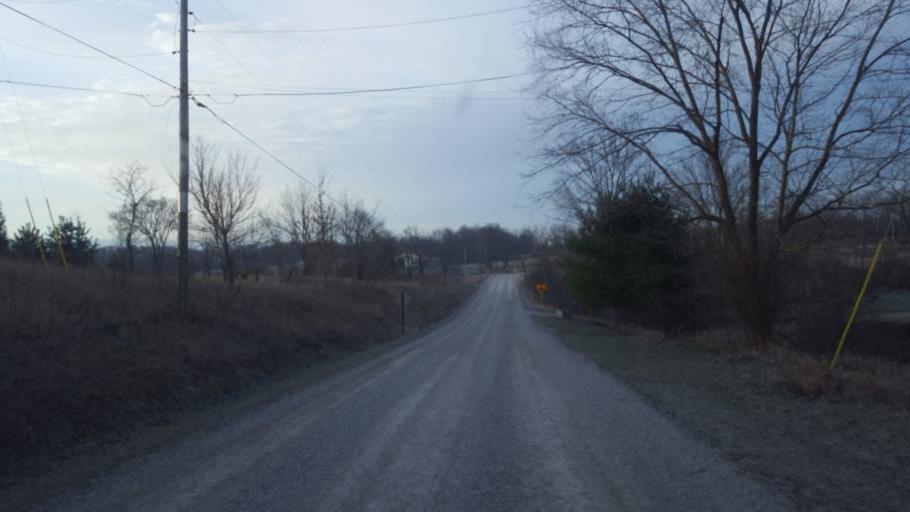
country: US
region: Ohio
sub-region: Morrow County
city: Mount Gilead
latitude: 40.4605
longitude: -82.7243
